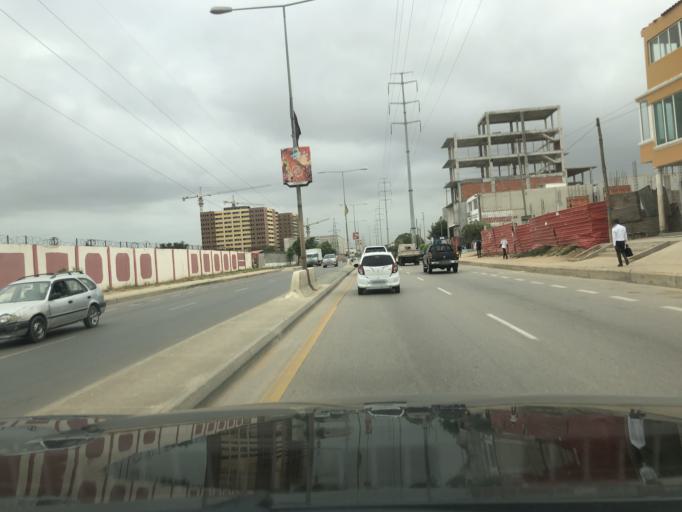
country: AO
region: Luanda
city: Luanda
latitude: -8.9724
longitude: 13.2092
